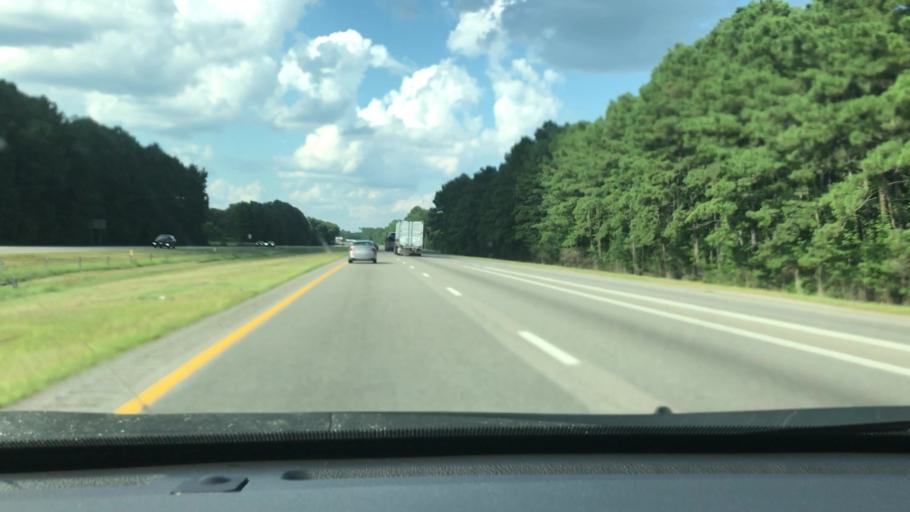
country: US
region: South Carolina
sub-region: Florence County
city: Timmonsville
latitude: 33.9501
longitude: -80.0535
